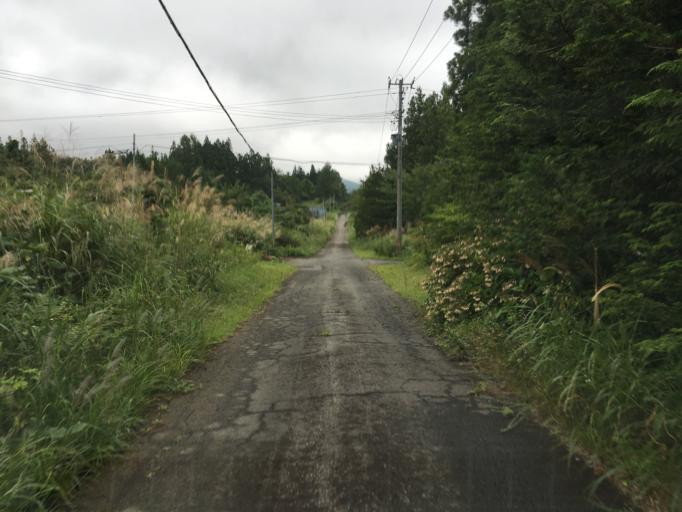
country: JP
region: Fukushima
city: Fukushima-shi
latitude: 37.8089
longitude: 140.3439
